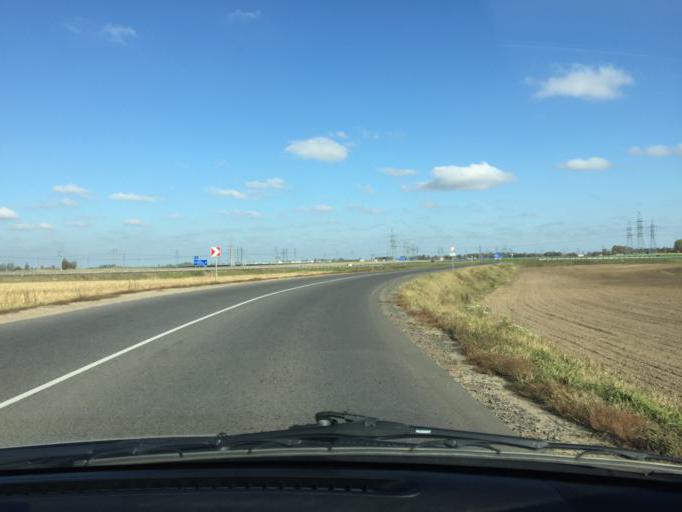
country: BY
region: Minsk
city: Slutsk
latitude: 53.0484
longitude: 27.5278
